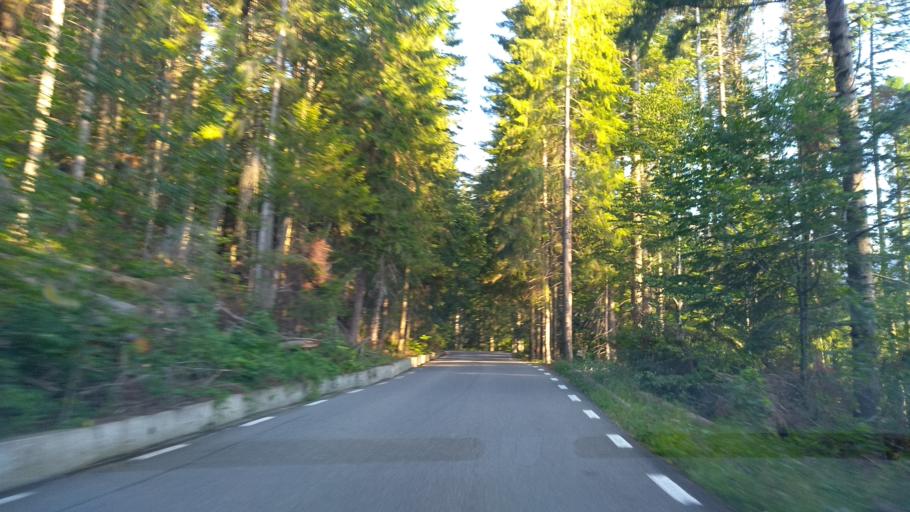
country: RO
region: Prahova
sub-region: Oras Sinaia
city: Sinaia
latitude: 45.3219
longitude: 25.5123
